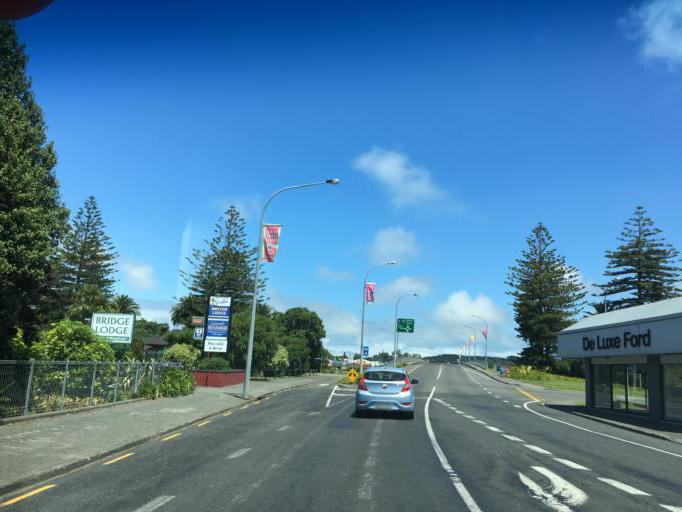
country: NZ
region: Hawke's Bay
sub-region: Wairoa District
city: Wairoa
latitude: -39.0298
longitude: 177.4191
